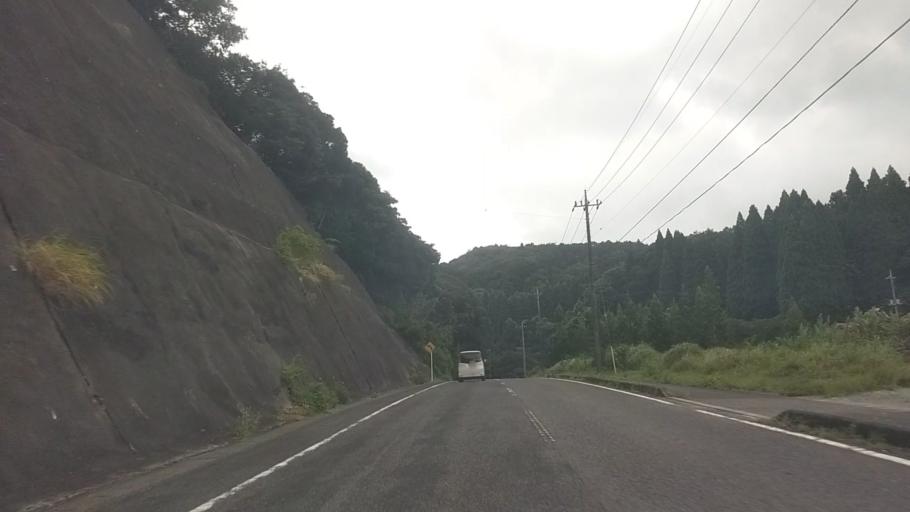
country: JP
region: Chiba
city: Kawaguchi
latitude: 35.2439
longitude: 140.1800
